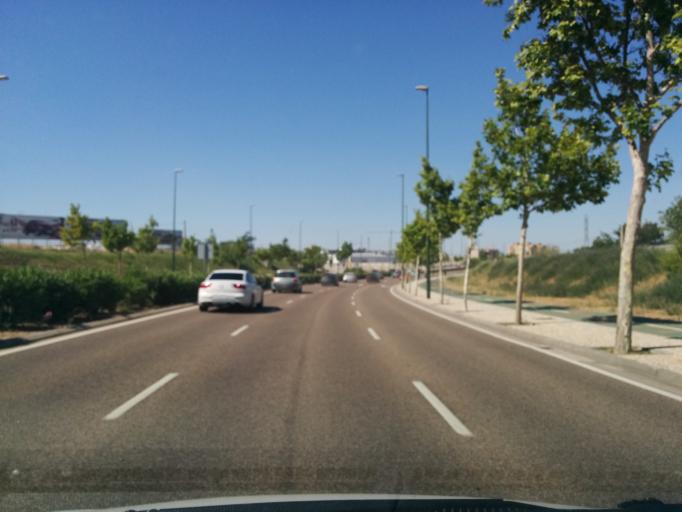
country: ES
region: Aragon
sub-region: Provincia de Zaragoza
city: Zaragoza
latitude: 41.6285
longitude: -0.8686
